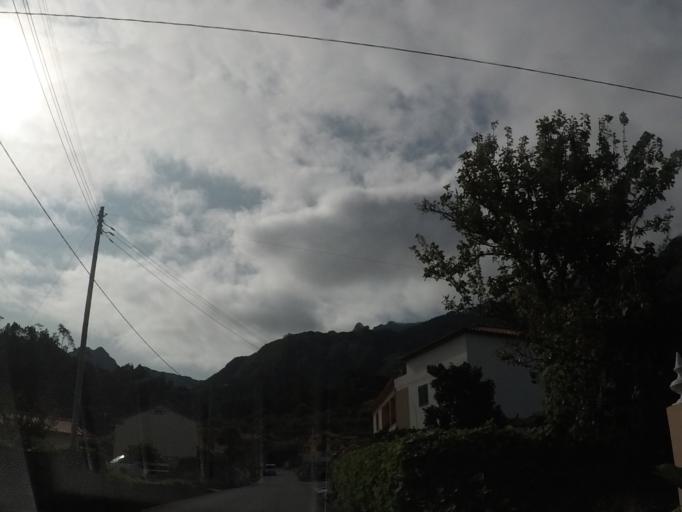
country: PT
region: Madeira
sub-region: Sao Vicente
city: Sao Vicente
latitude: 32.7824
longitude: -17.0438
